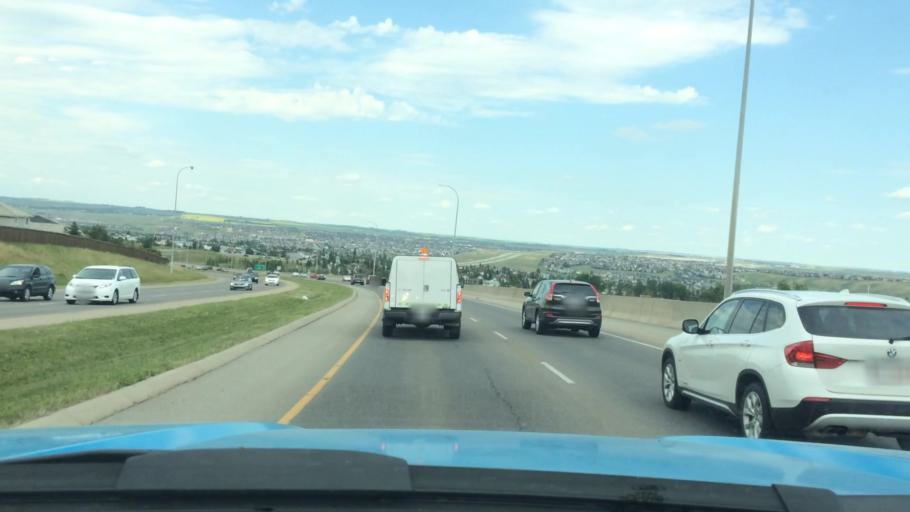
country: CA
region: Alberta
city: Calgary
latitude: 51.1363
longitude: -114.1213
